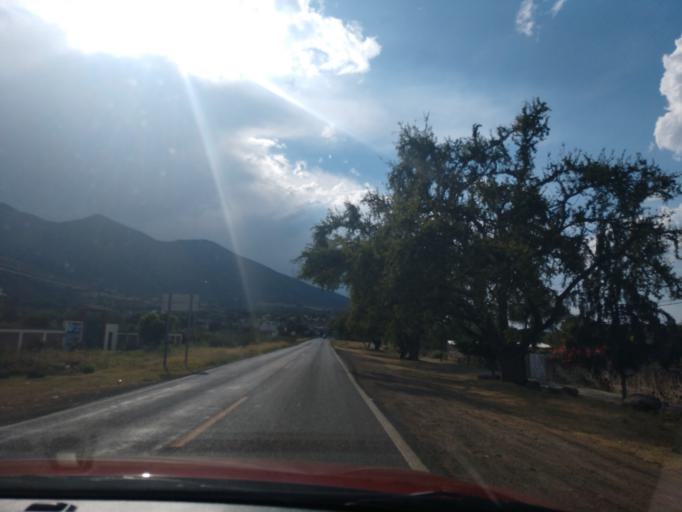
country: MX
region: Jalisco
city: San Juan Cosala
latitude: 20.1944
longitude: -103.2996
